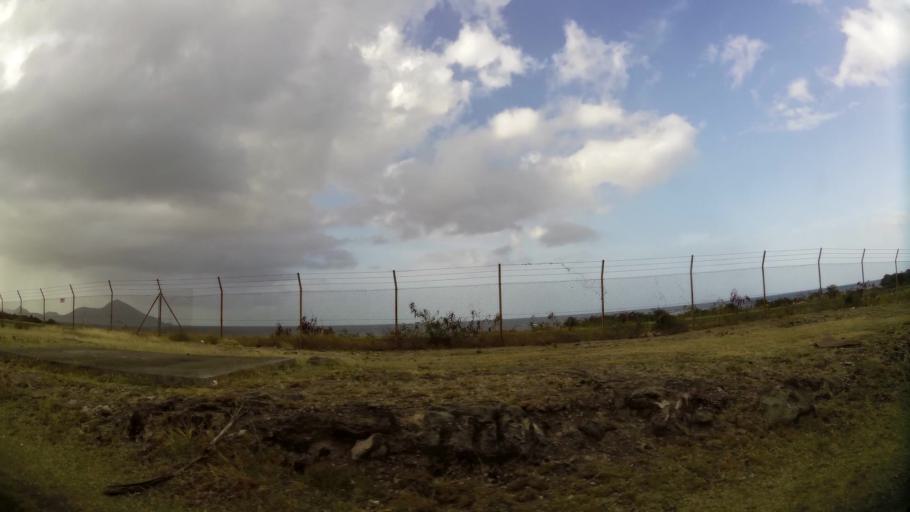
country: KN
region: Saint James Windwa
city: Newcastle
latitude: 17.2052
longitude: -62.5851
